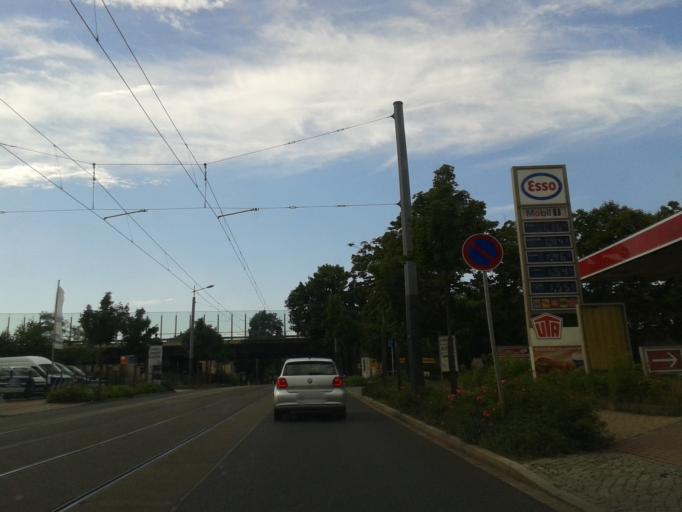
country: DE
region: Saxony
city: Radebeul
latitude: 51.0936
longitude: 13.6982
